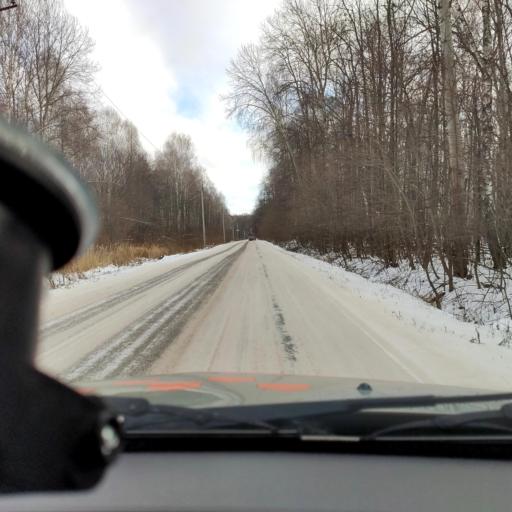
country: RU
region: Bashkortostan
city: Avdon
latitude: 54.7825
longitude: 55.7430
